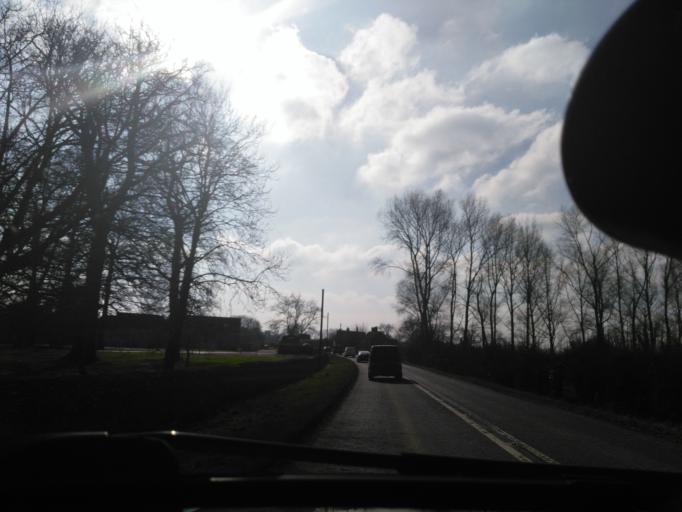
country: GB
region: England
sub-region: Wiltshire
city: Malmesbury
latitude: 51.6044
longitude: -2.0864
